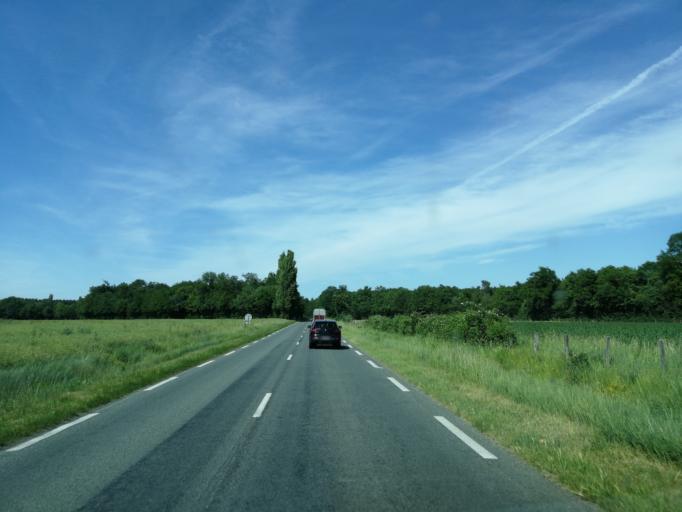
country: FR
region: Centre
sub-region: Departement d'Indre-et-Loire
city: Ligre
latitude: 47.0947
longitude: 0.1861
